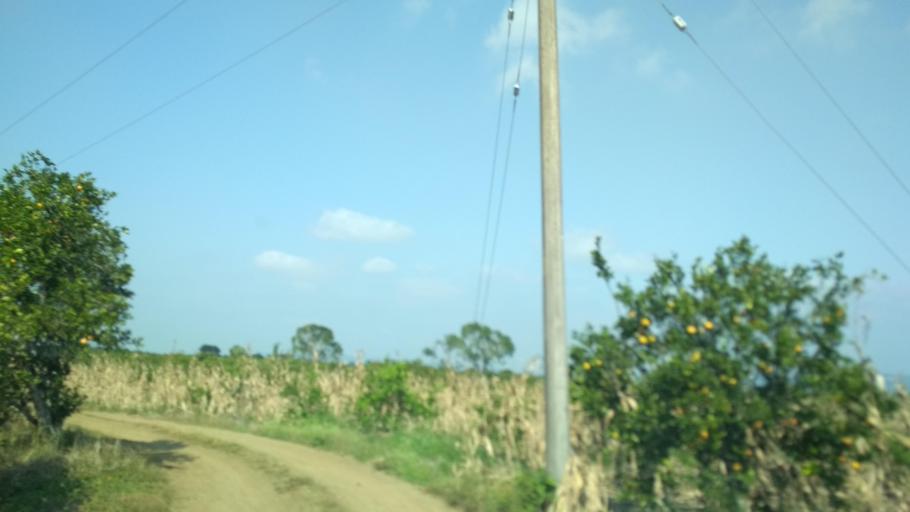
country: MX
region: Puebla
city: San Jose Acateno
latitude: 20.2035
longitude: -97.1800
